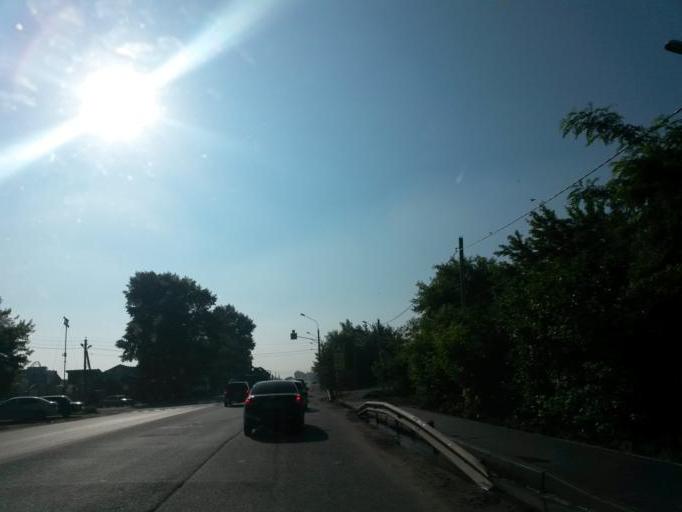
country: RU
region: Moskovskaya
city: Yam
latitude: 55.4856
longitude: 37.7524
